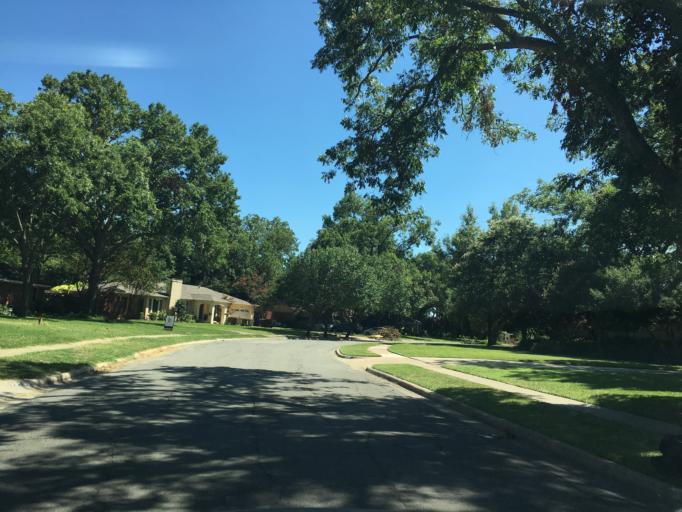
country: US
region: Texas
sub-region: Dallas County
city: Highland Park
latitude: 32.8379
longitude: -96.6986
